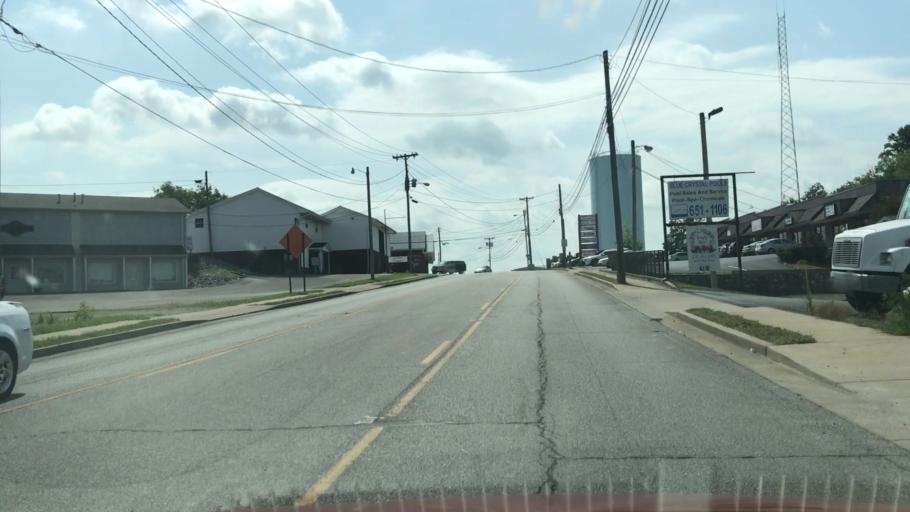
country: US
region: Kentucky
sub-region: Barren County
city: Glasgow
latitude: 37.0005
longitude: -85.9239
